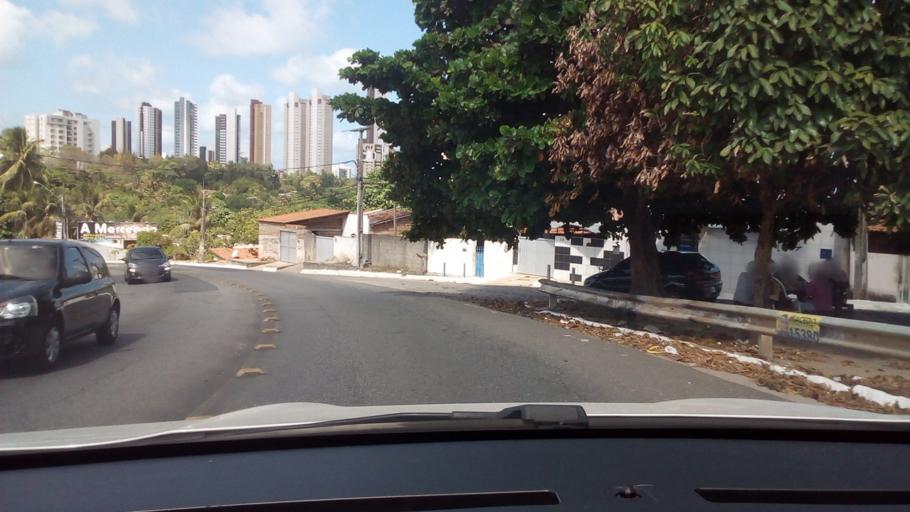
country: BR
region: Paraiba
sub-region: Joao Pessoa
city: Joao Pessoa
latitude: -7.1290
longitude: -34.8372
